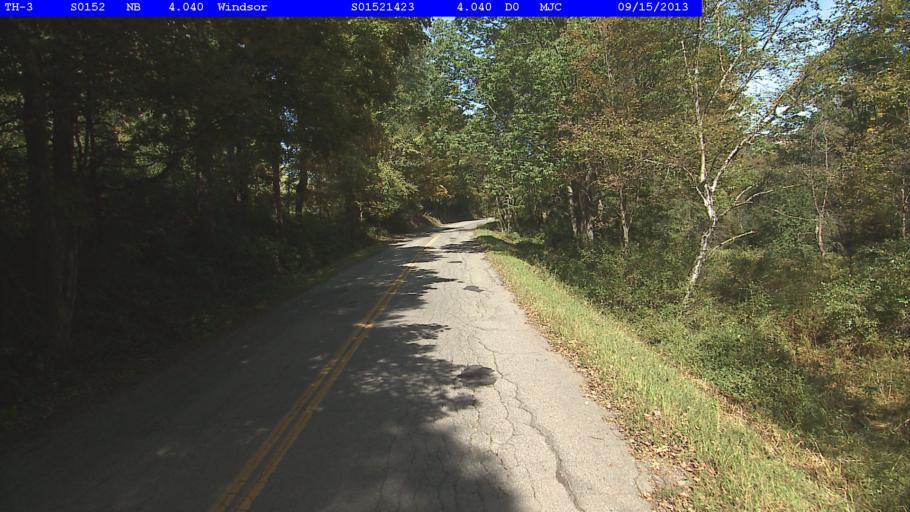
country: US
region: Vermont
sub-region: Windsor County
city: Windsor
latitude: 43.5188
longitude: -72.4328
